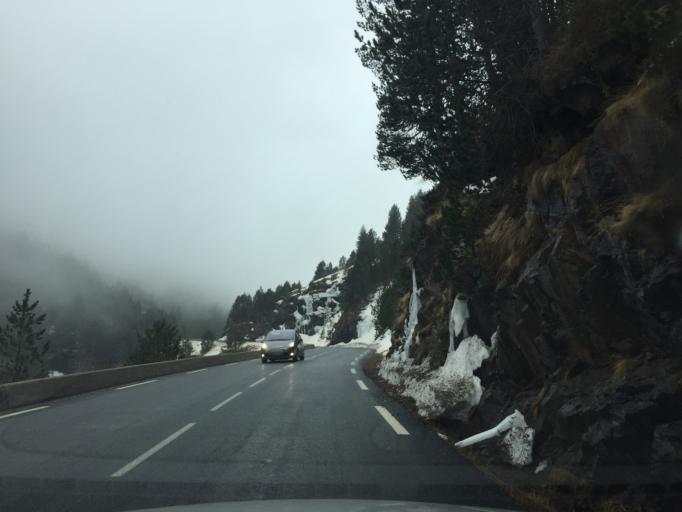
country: FR
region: Midi-Pyrenees
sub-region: Departement des Hautes-Pyrenees
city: Saint-Lary-Soulan
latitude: 42.7715
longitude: 0.1991
